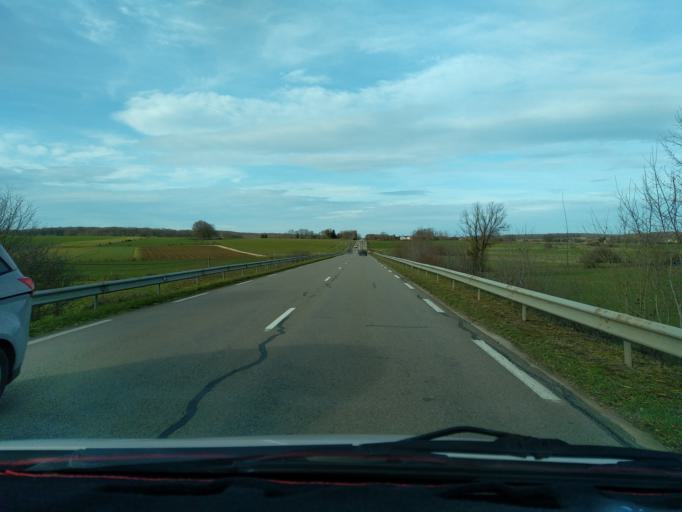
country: FR
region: Franche-Comte
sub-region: Departement de la Haute-Saone
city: Gray
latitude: 47.3669
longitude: 5.6700
